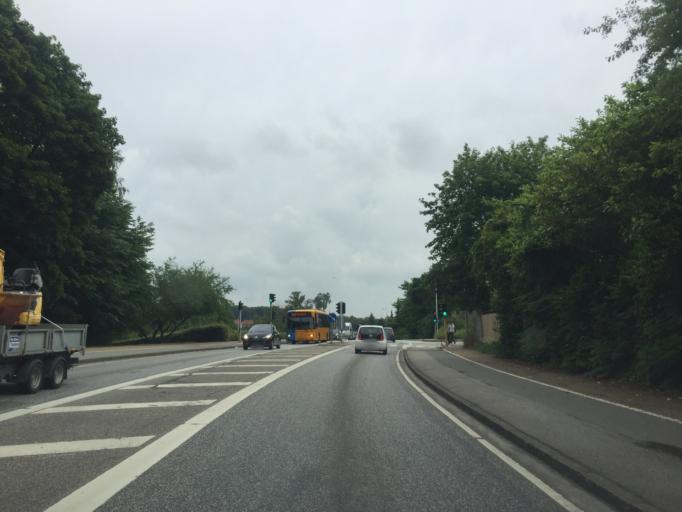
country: DK
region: Capital Region
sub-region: Rudersdal Kommune
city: Birkerod
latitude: 55.8251
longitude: 12.4256
